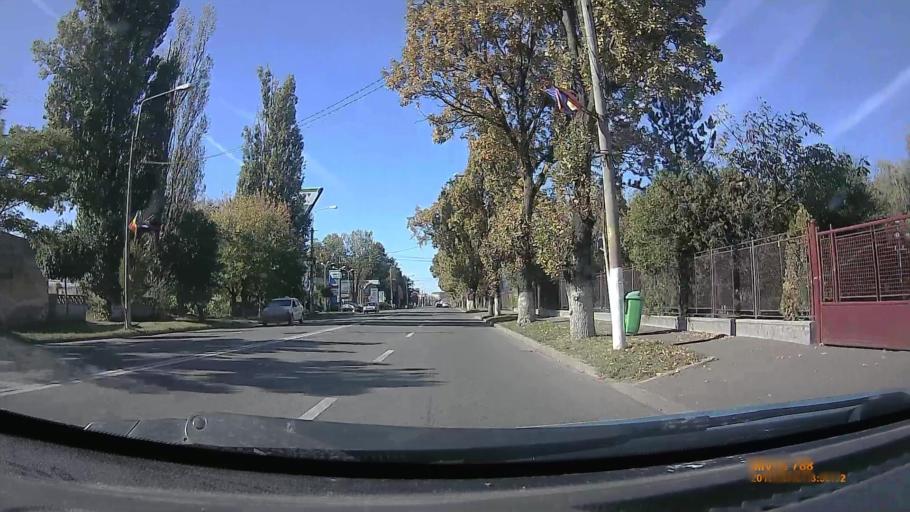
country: RO
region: Bihor
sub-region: Comuna Sanmartin
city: Sanmartin
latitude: 47.0408
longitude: 21.9766
